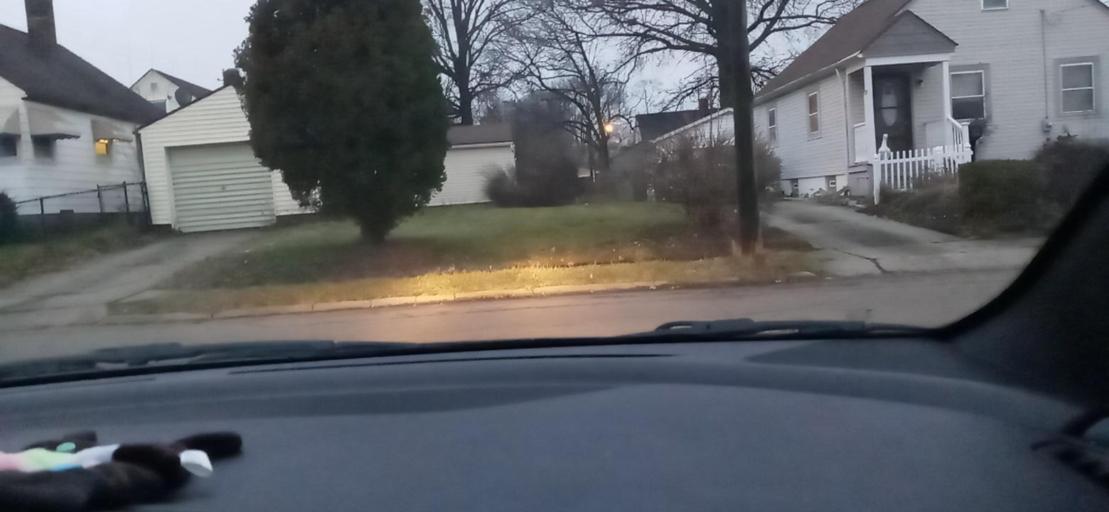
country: US
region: Ohio
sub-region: Summit County
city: Portage Lakes
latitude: 41.0401
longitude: -81.5030
